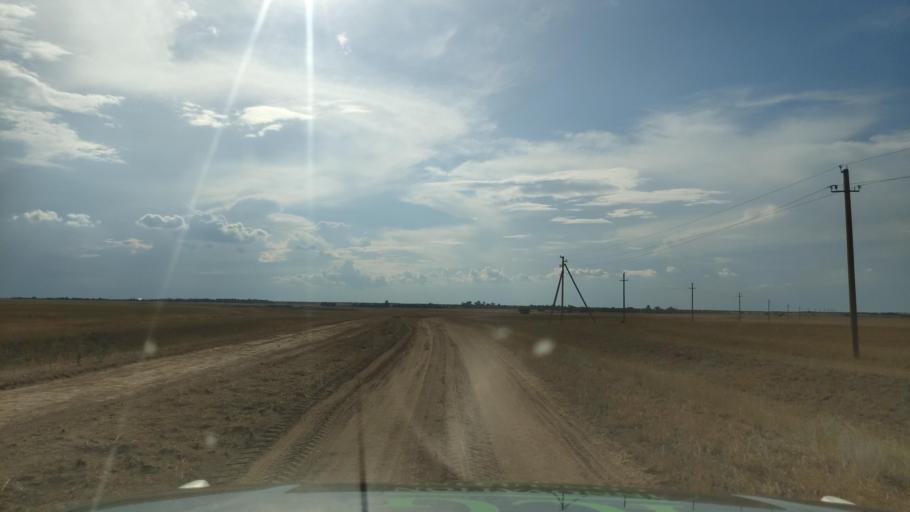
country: KZ
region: Pavlodar
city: Pavlodar
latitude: 52.5130
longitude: 77.4671
